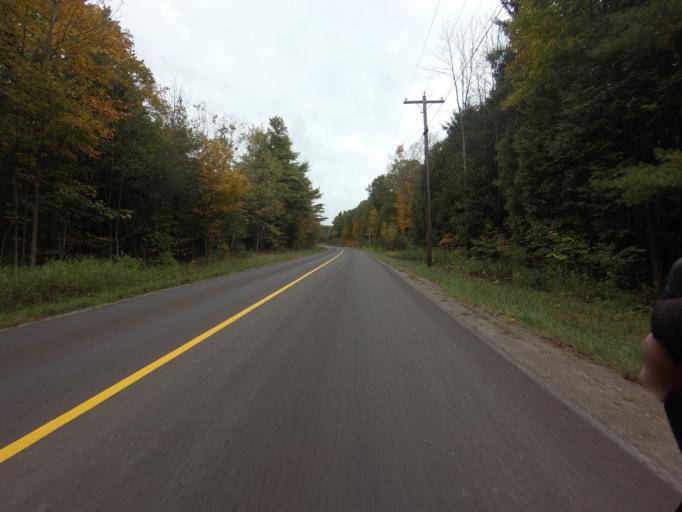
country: CA
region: Ontario
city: Gananoque
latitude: 44.5780
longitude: -76.0860
